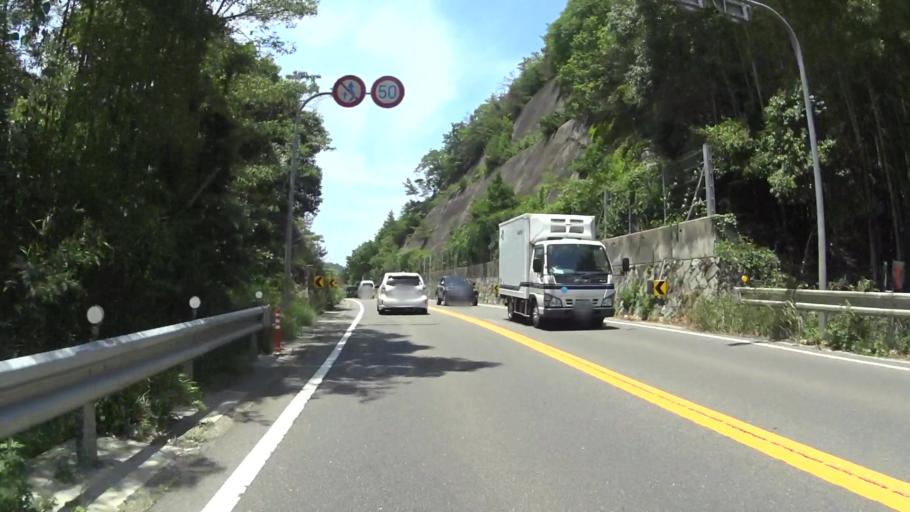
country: JP
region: Kyoto
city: Kameoka
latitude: 35.0809
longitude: 135.5160
